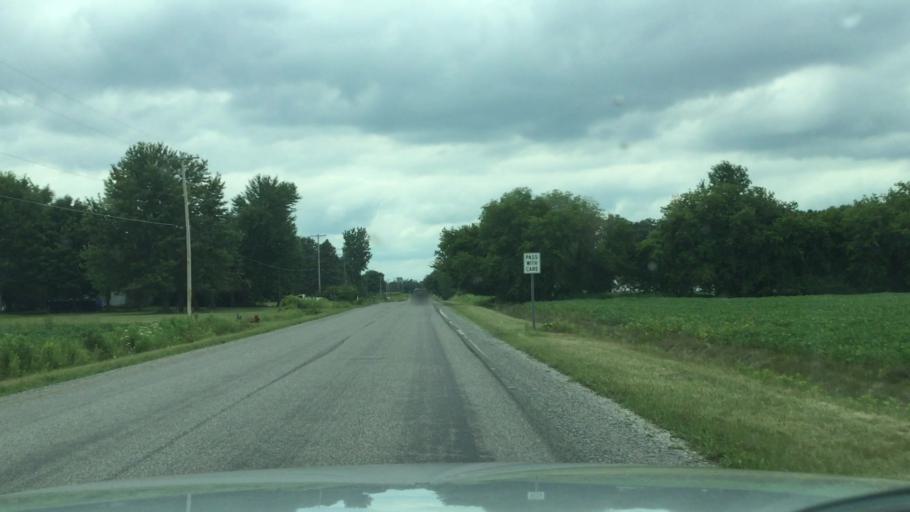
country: US
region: Michigan
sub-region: Saginaw County
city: Birch Run
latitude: 43.2507
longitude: -83.8457
